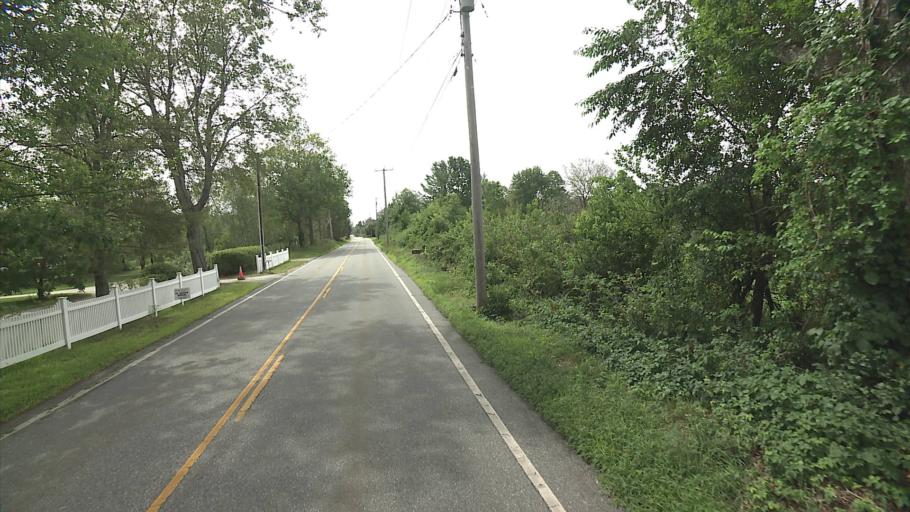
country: US
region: Connecticut
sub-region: Windham County
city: Thompson
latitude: 42.0006
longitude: -71.8458
